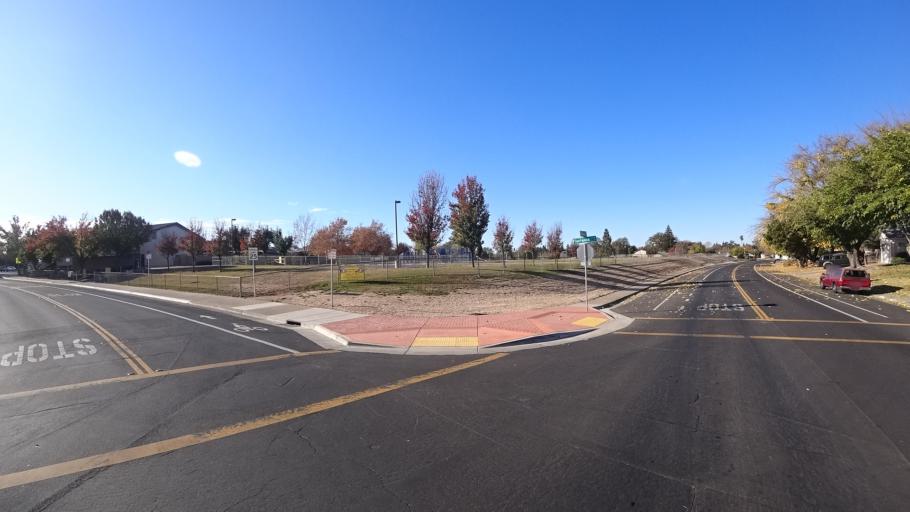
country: US
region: California
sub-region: Sacramento County
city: Fair Oaks
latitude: 38.6675
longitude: -121.2946
